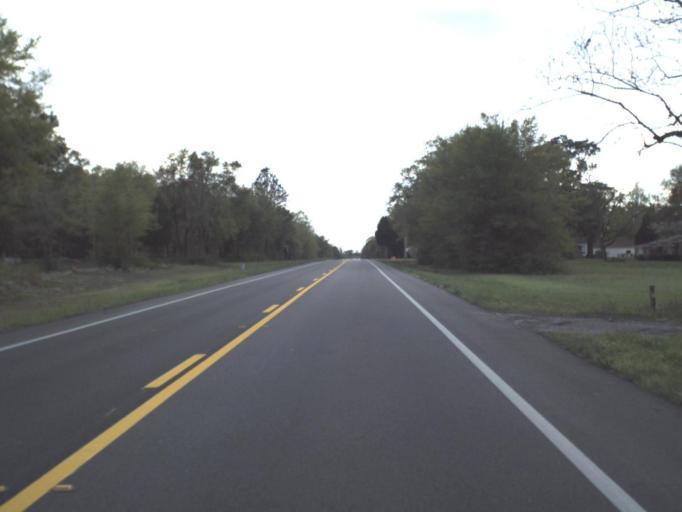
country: US
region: Florida
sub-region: Okaloosa County
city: Crestview
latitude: 30.8759
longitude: -86.5156
